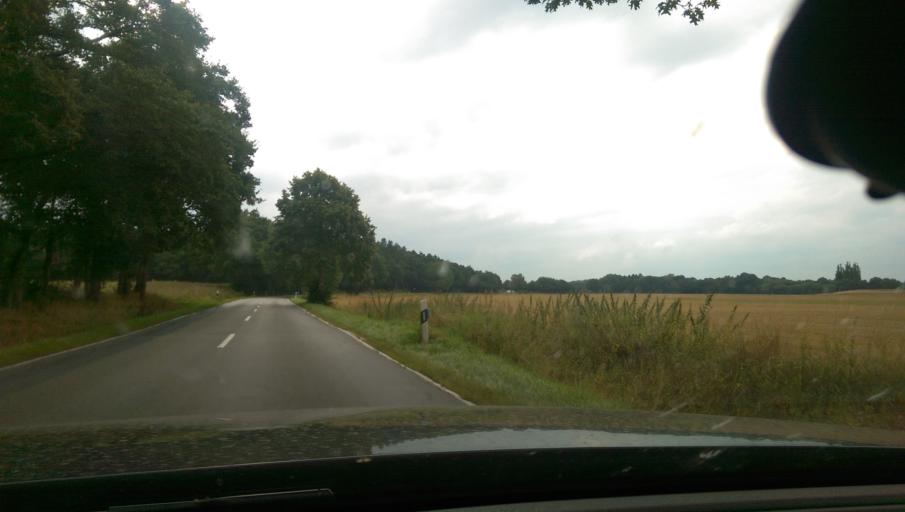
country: DE
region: Lower Saxony
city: Neustadt am Rubenberge
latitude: 52.5691
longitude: 9.5563
